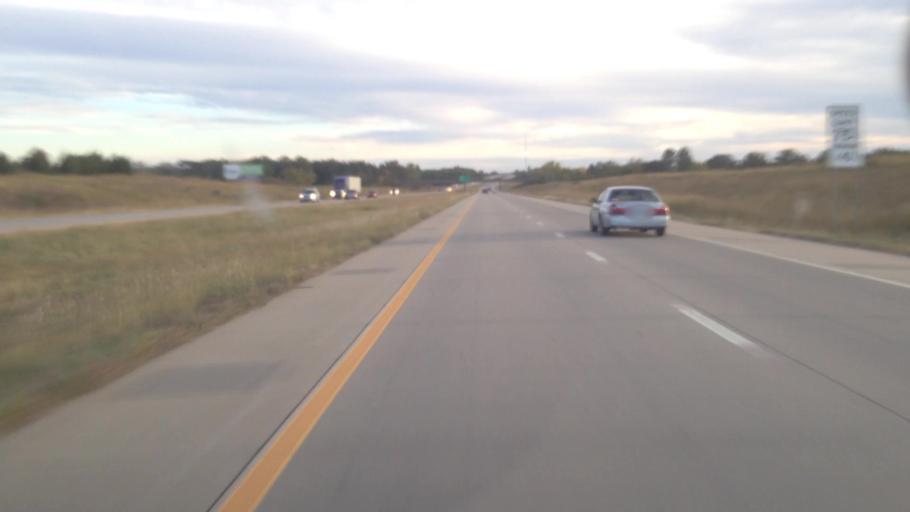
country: US
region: Kansas
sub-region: Franklin County
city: Ottawa
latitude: 38.6136
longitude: -95.2326
